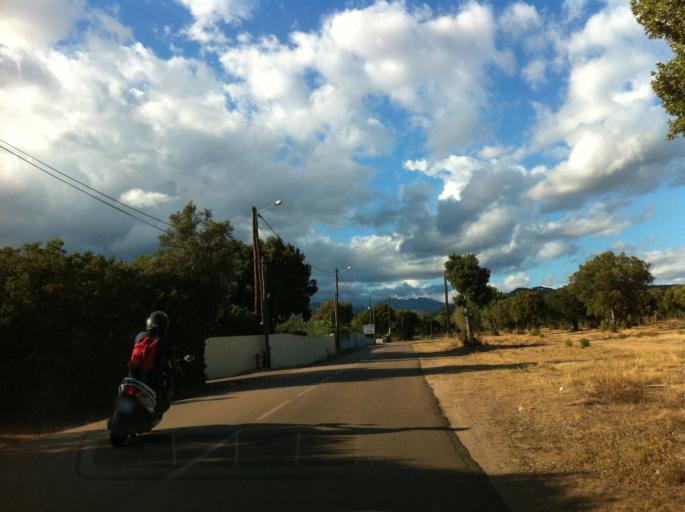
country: FR
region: Corsica
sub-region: Departement de la Corse-du-Sud
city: Porto-Vecchio
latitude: 41.6438
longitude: 9.3294
